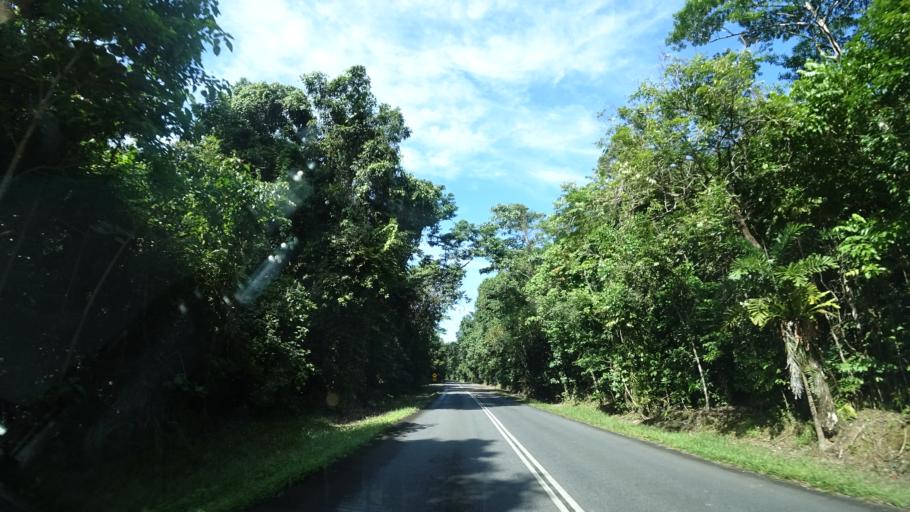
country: AU
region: Queensland
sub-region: Cairns
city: Port Douglas
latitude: -16.1504
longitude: 145.4410
